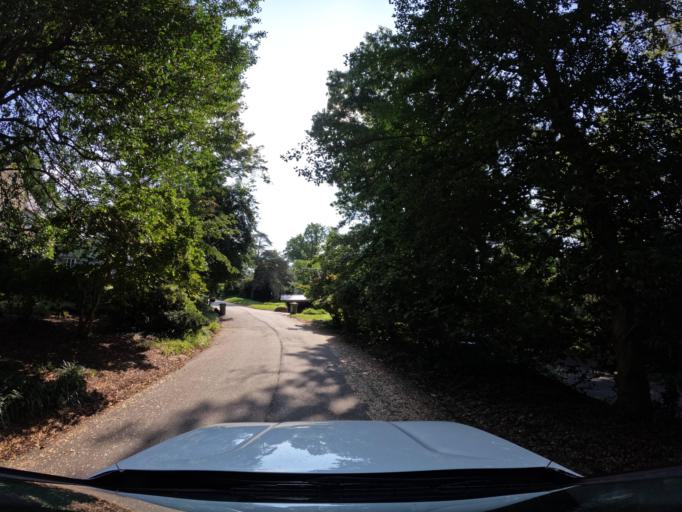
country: US
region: Maryland
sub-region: Baltimore County
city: Towson
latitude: 39.3687
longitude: -76.6440
